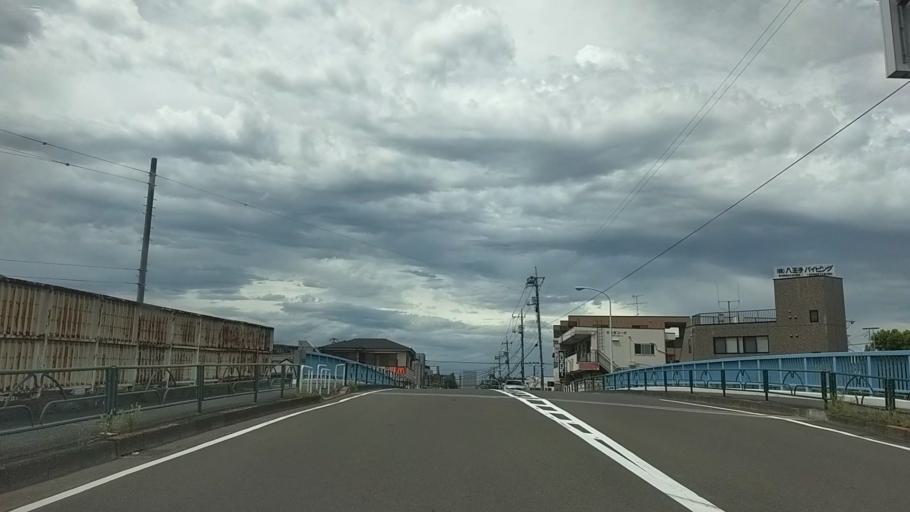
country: JP
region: Tokyo
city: Hachioji
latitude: 35.6444
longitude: 139.3611
